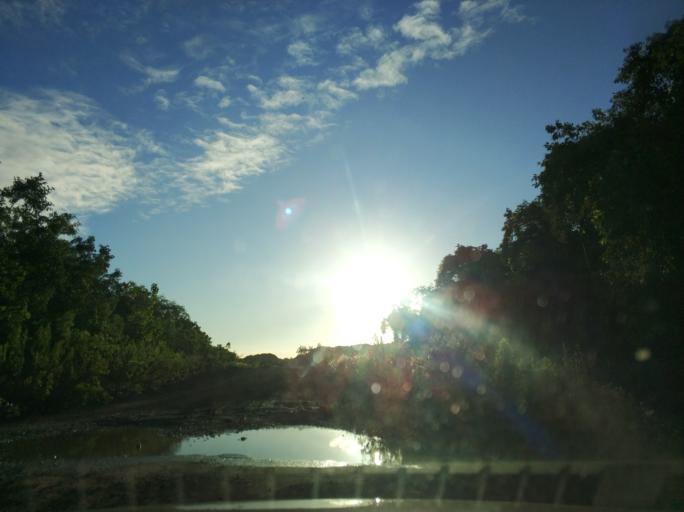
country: US
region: Hawaii
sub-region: Hawaii County
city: Leilani Estates
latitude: 19.3612
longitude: -154.9778
